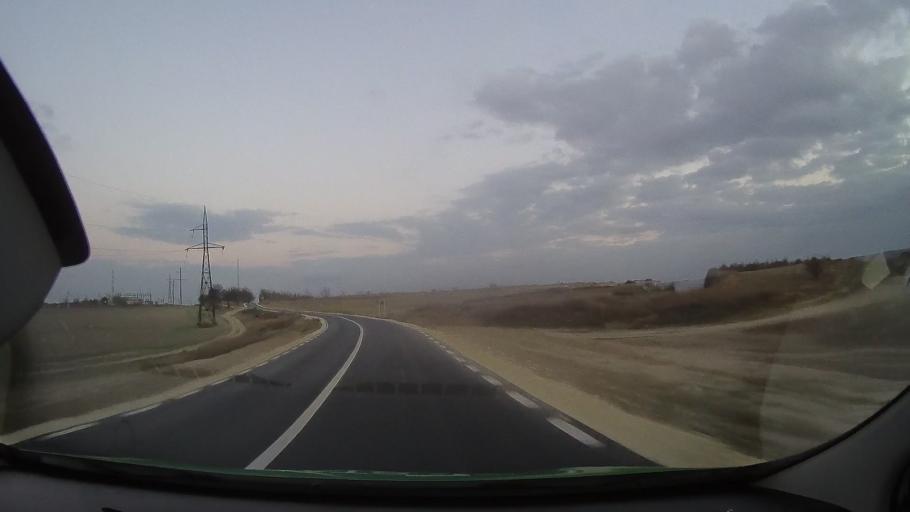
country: RO
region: Constanta
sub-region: Comuna Baneasa
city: Baneasa
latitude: 44.0806
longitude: 27.6896
